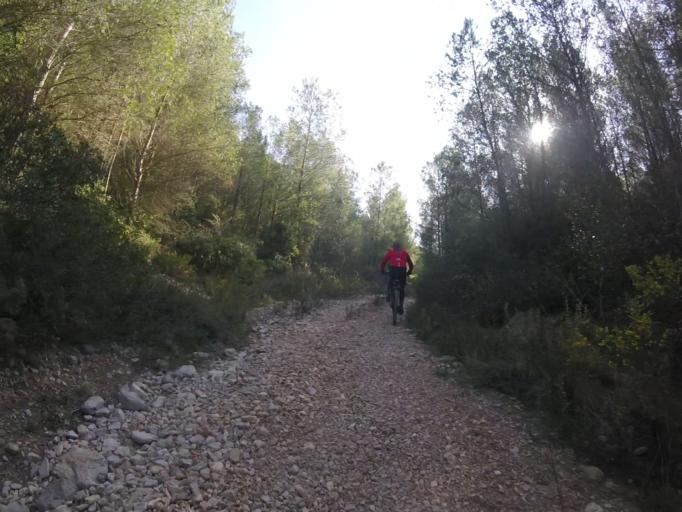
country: ES
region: Valencia
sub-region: Provincia de Castello
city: Santa Magdalena de Pulpis
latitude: 40.3097
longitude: 0.3337
